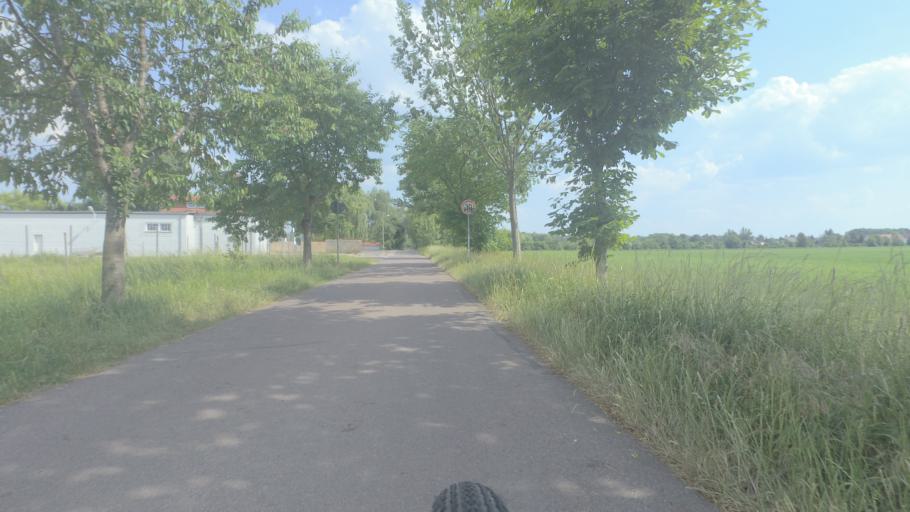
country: DE
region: Saxony-Anhalt
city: Koethen
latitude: 51.7668
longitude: 11.9305
